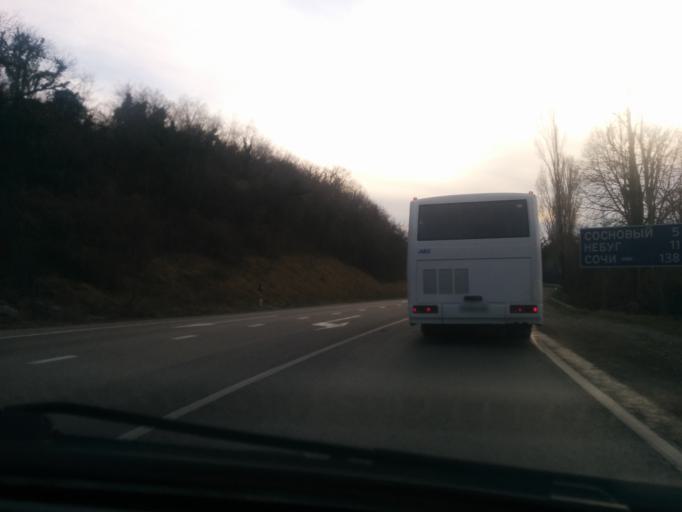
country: RU
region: Krasnodarskiy
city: Ol'ginka
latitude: 44.1946
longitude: 38.8914
